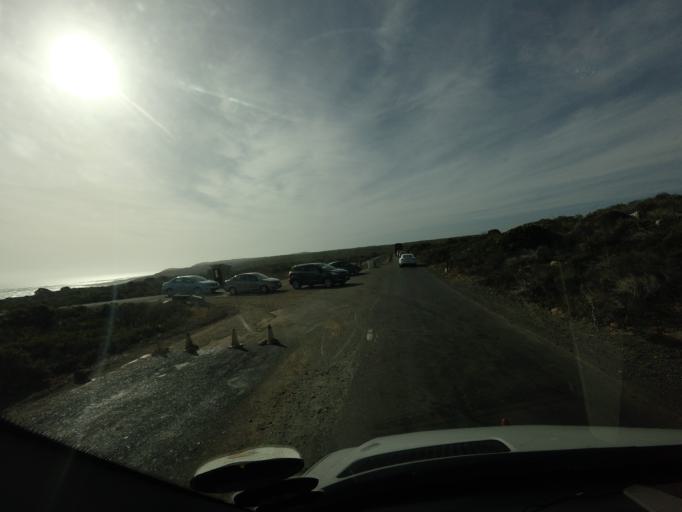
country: ZA
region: Western Cape
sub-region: City of Cape Town
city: Retreat
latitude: -34.3377
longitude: 18.4651
